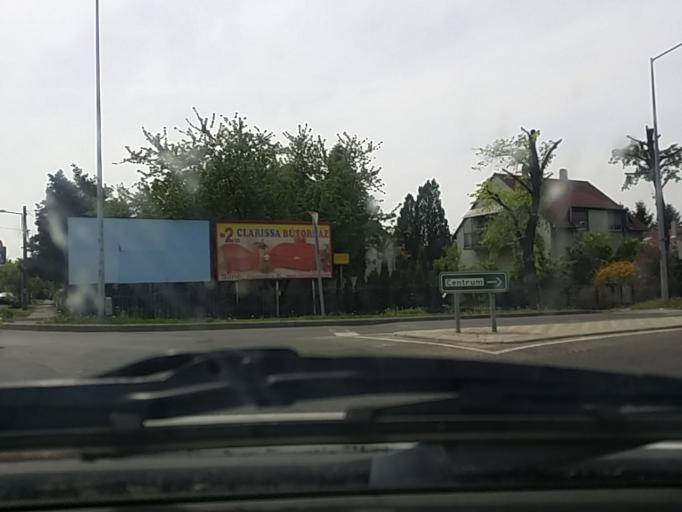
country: HU
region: Zala
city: Nagykanizsa
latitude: 46.4527
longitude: 17.0093
